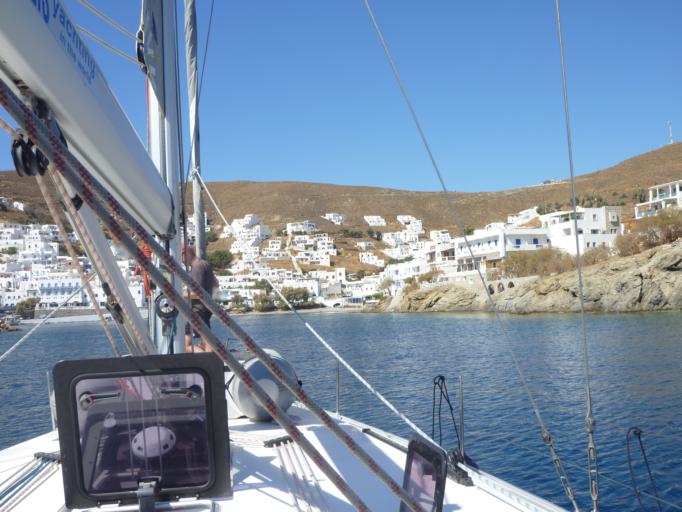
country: GR
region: South Aegean
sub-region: Nomos Dodekanisou
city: Astypalaia
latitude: 36.5484
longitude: 26.3544
